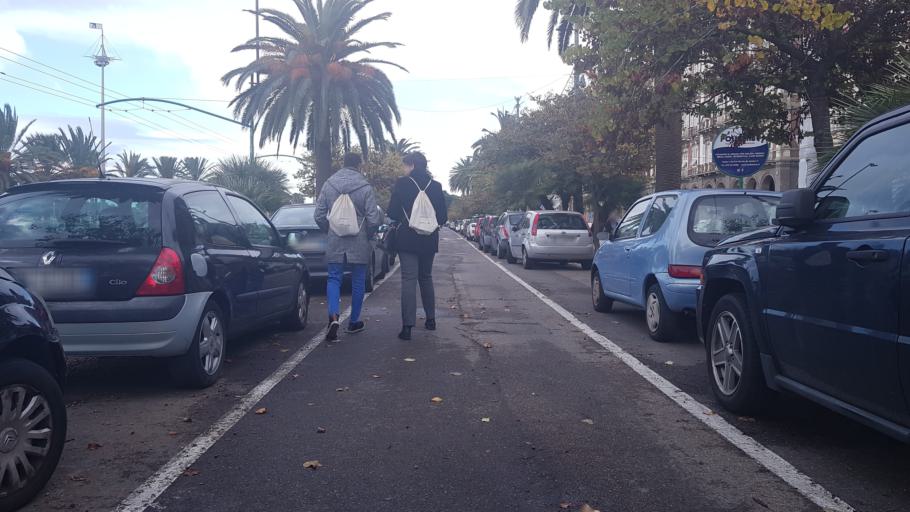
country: IT
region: Sardinia
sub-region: Provincia di Cagliari
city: Cagliari
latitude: 39.2131
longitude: 9.1136
